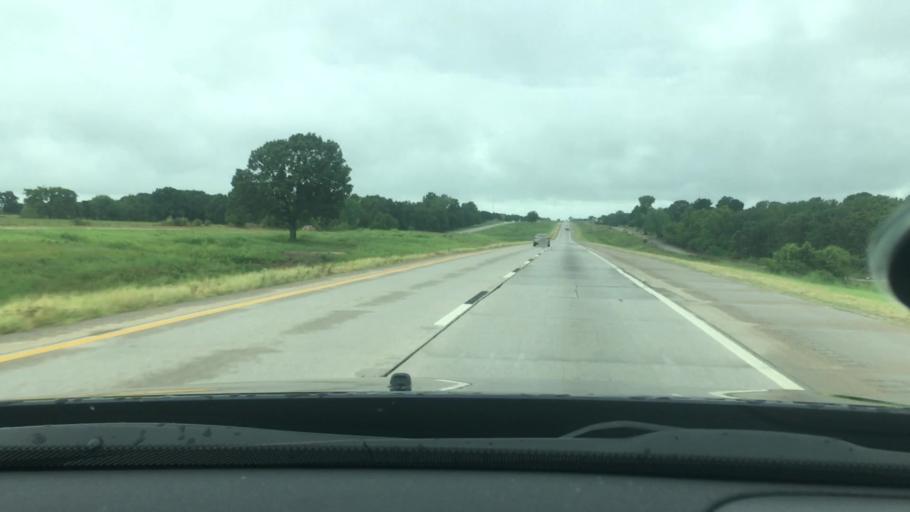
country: US
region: Oklahoma
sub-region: Atoka County
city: Atoka
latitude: 34.2145
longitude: -96.2319
